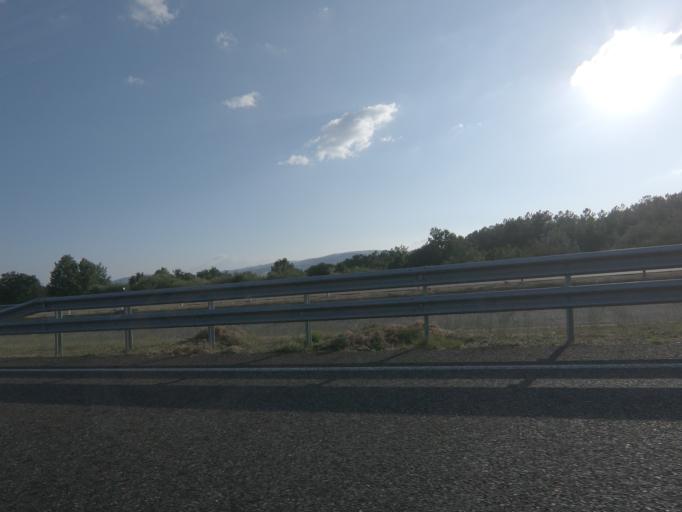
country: ES
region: Galicia
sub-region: Provincia de Ourense
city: Verin
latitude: 41.8985
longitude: -7.4247
